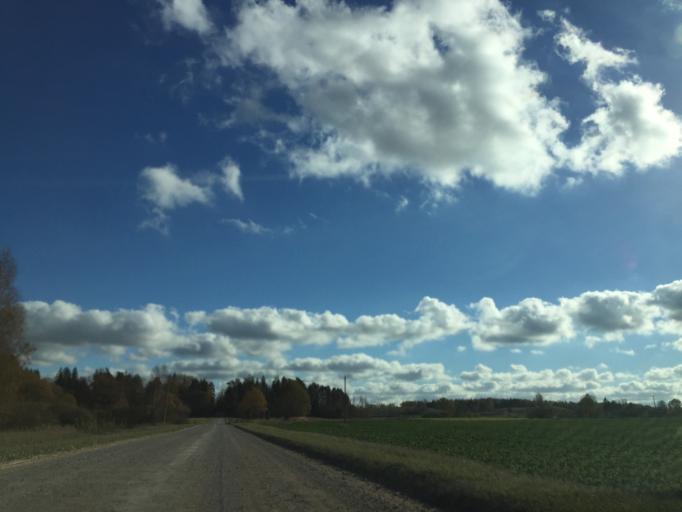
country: LV
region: Tukuma Rajons
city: Tukums
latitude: 56.9664
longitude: 22.9668
